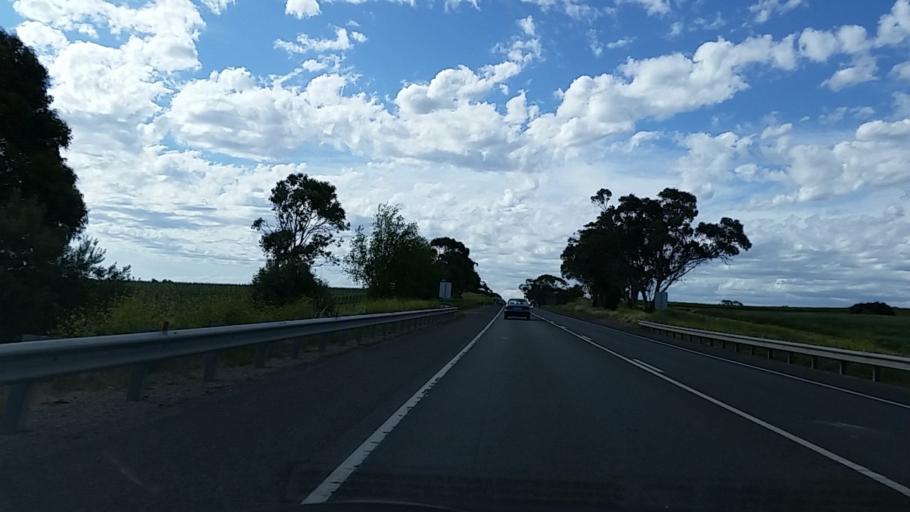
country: AU
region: South Australia
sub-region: Onkaparinga
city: McLaren Vale
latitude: -35.2199
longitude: 138.5243
